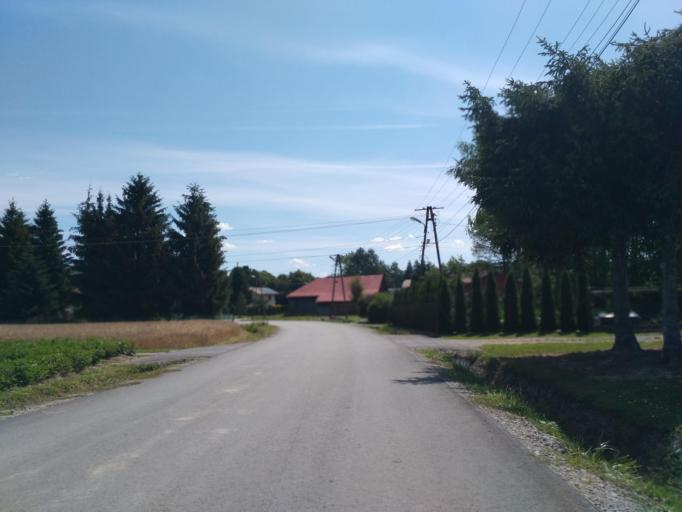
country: PL
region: Subcarpathian Voivodeship
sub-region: Powiat brzozowski
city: Jablonica Polska
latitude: 49.6927
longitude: 21.8728
